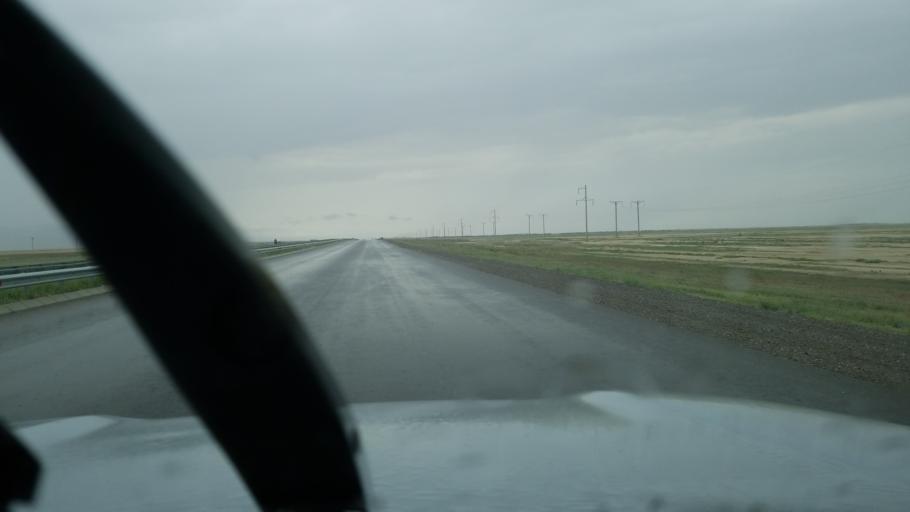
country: TM
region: Balkan
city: Serdar
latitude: 39.0250
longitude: 56.1972
